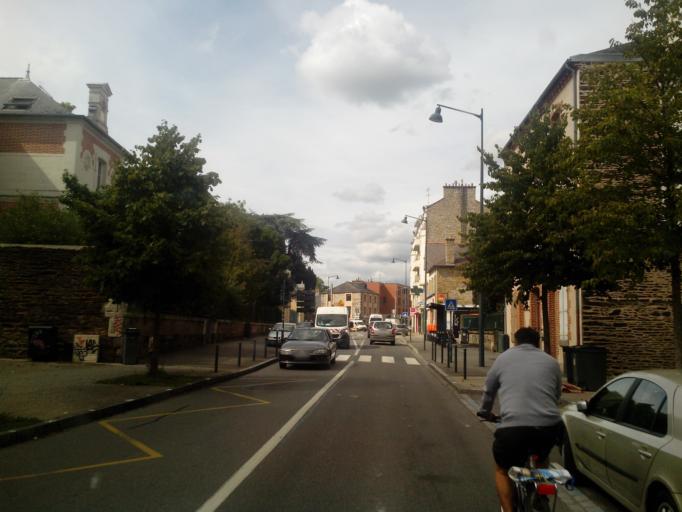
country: FR
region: Brittany
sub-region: Departement d'Ille-et-Vilaine
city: Rennes
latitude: 48.1216
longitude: -1.6832
